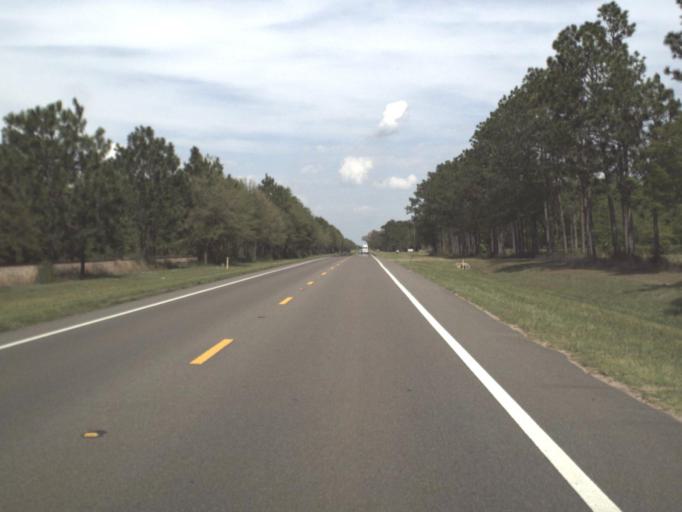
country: US
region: Florida
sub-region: Santa Rosa County
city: East Milton
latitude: 30.6450
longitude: -86.9281
